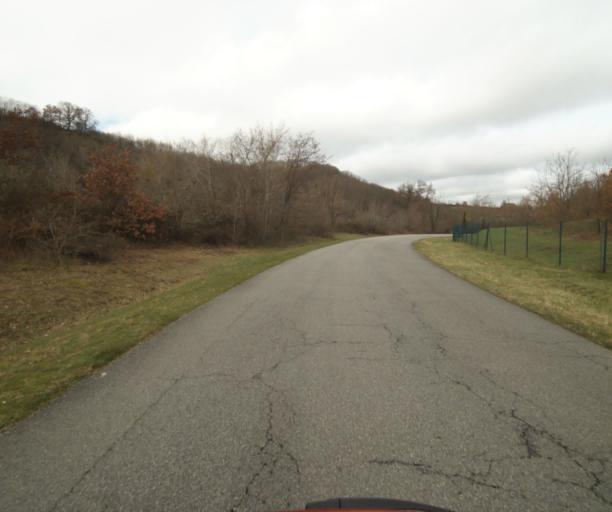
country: FR
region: Midi-Pyrenees
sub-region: Departement de l'Ariege
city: Pamiers
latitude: 43.1197
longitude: 1.5974
